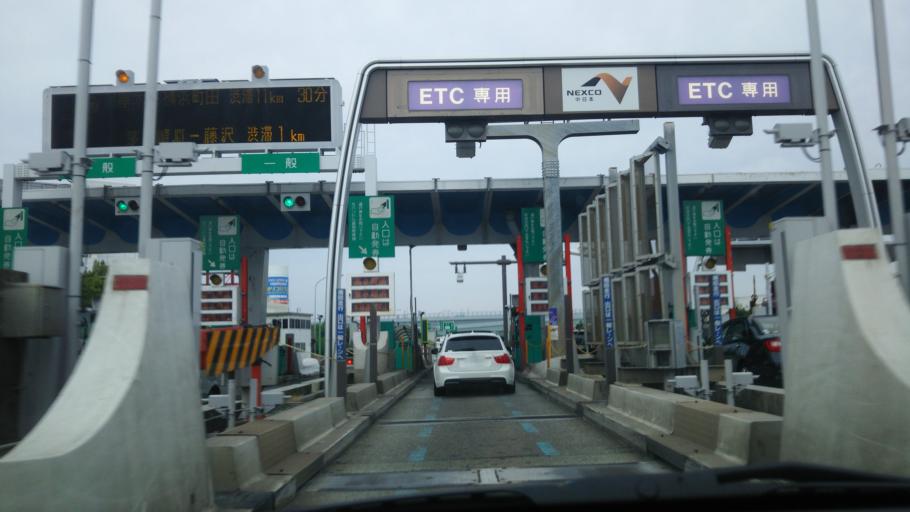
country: JP
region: Kanagawa
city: Atsugi
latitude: 35.4211
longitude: 139.3622
